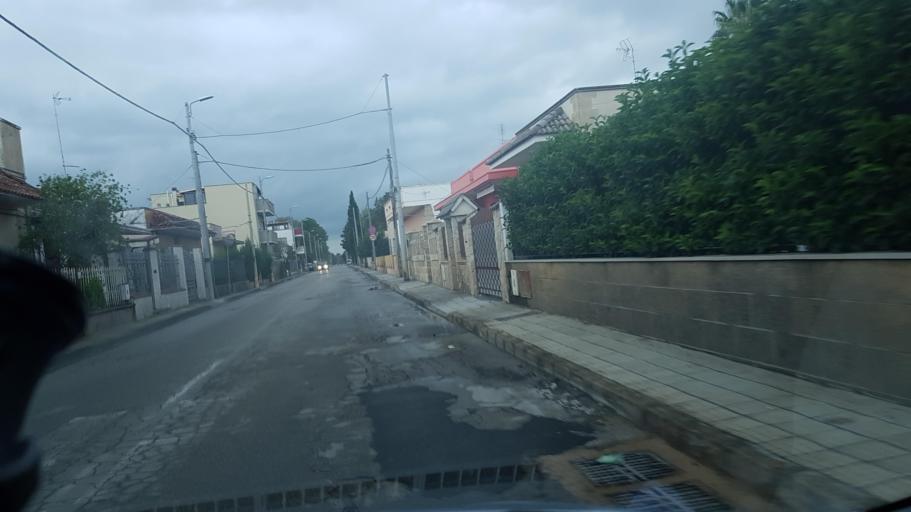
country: IT
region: Apulia
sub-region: Provincia di Lecce
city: Magliano
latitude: 40.3642
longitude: 18.0777
